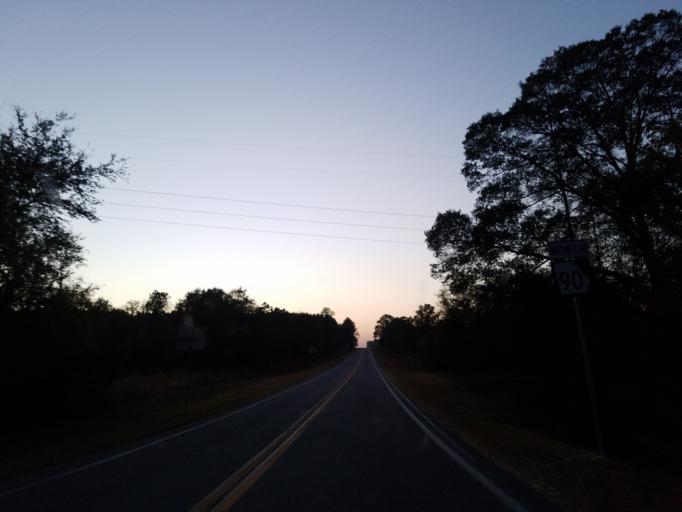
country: US
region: Georgia
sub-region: Wilcox County
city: Rochelle
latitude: 31.8533
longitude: -83.5593
